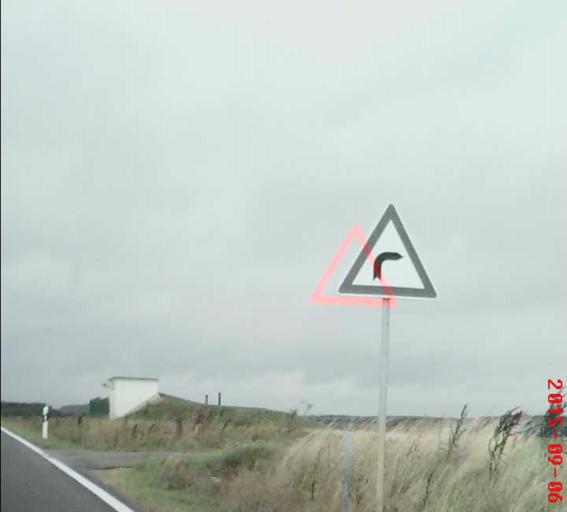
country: DE
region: Thuringia
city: Muehlhausen
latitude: 51.2559
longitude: 10.4518
